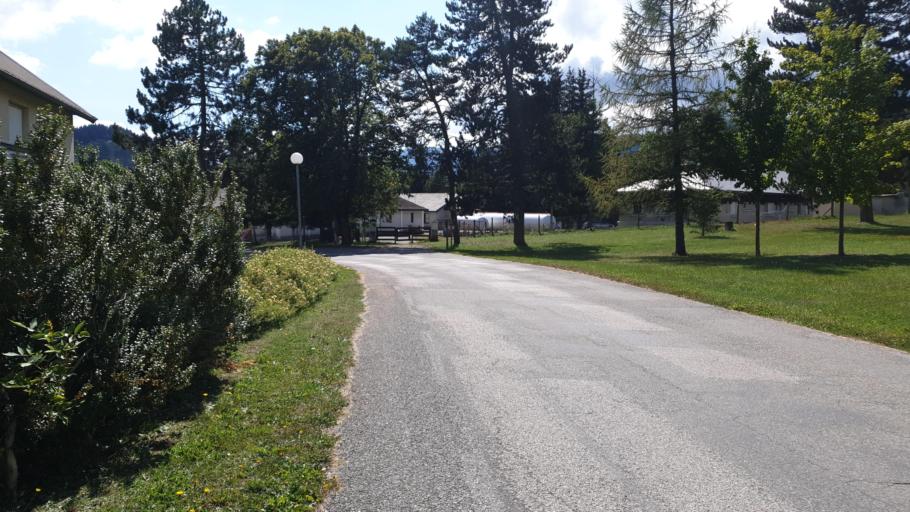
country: FR
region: Rhone-Alpes
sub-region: Departement de l'Isere
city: Autrans
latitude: 45.1818
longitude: 5.5534
